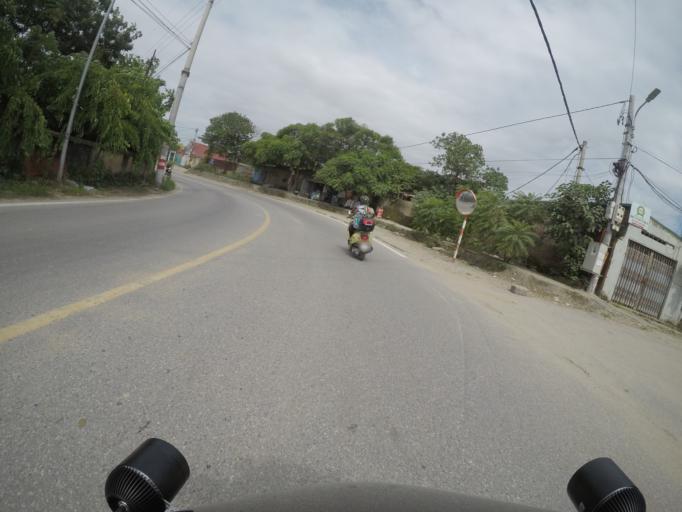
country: VN
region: Ha Noi
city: Tay Ho
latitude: 21.0914
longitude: 105.7697
